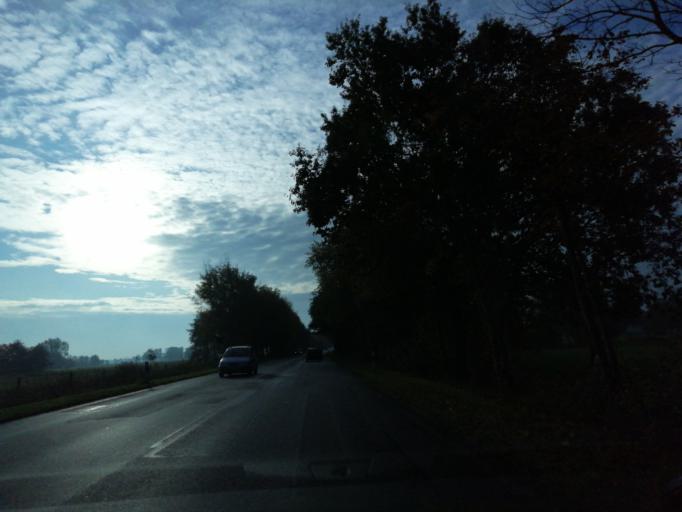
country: DE
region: Lower Saxony
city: Fedderwarden
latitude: 53.6002
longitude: 8.0497
